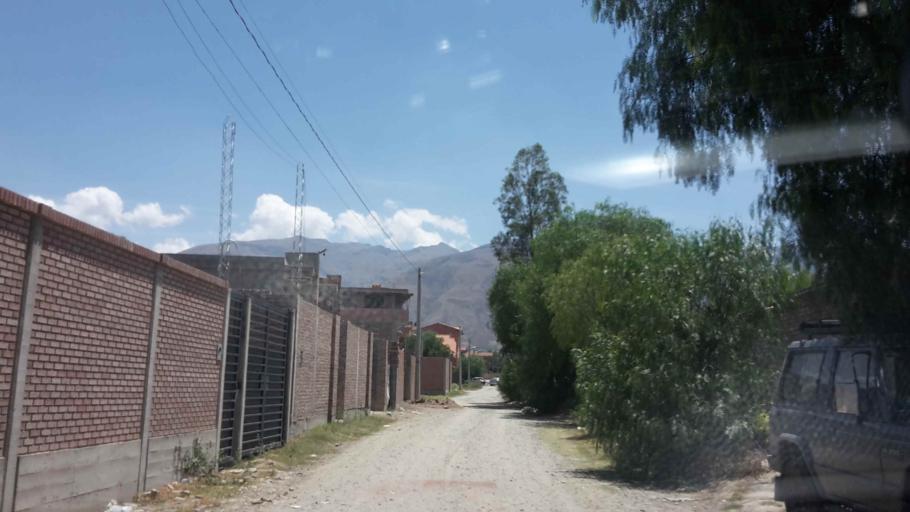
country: BO
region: Cochabamba
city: Cochabamba
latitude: -17.3708
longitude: -66.1937
